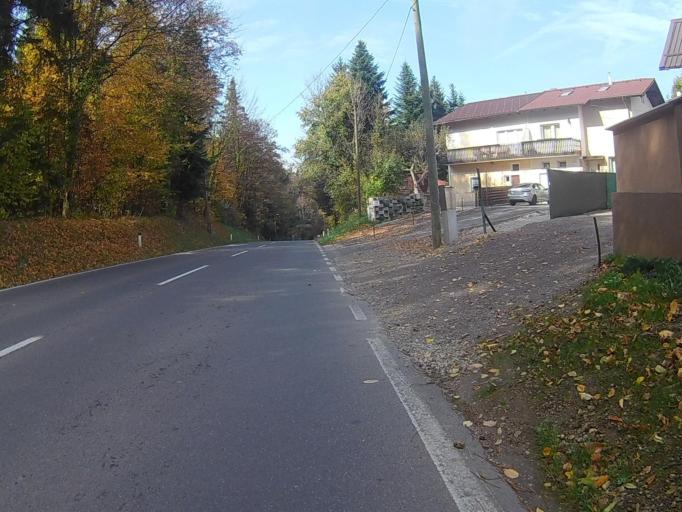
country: SI
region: Selnica ob Dravi
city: Selnica ob Dravi
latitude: 46.5414
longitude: 15.5026
